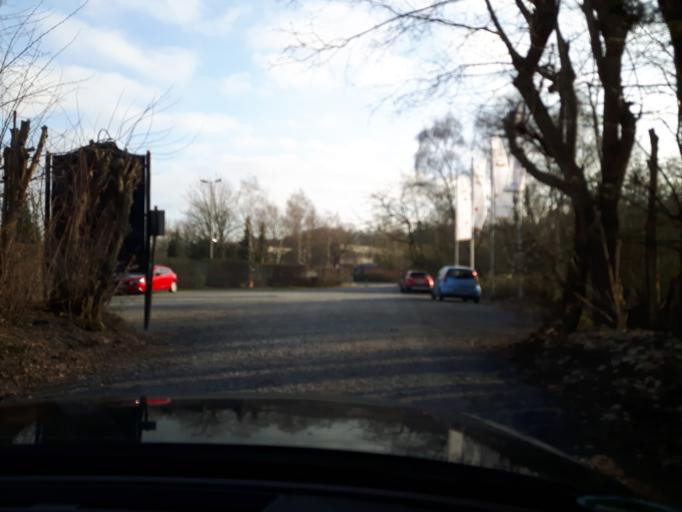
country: DE
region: North Rhine-Westphalia
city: Hattingen
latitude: 51.4035
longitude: 7.1755
